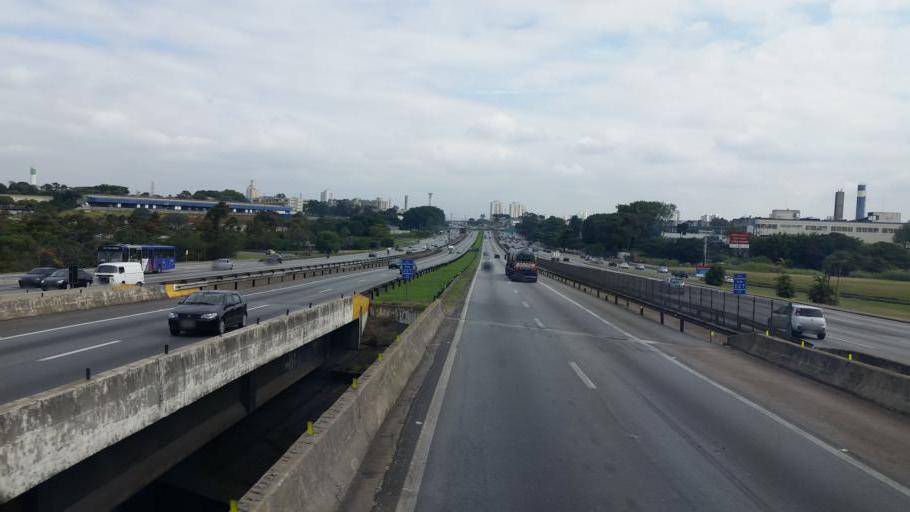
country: BR
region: Sao Paulo
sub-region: Guarulhos
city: Guarulhos
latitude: -23.4981
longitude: -46.5593
